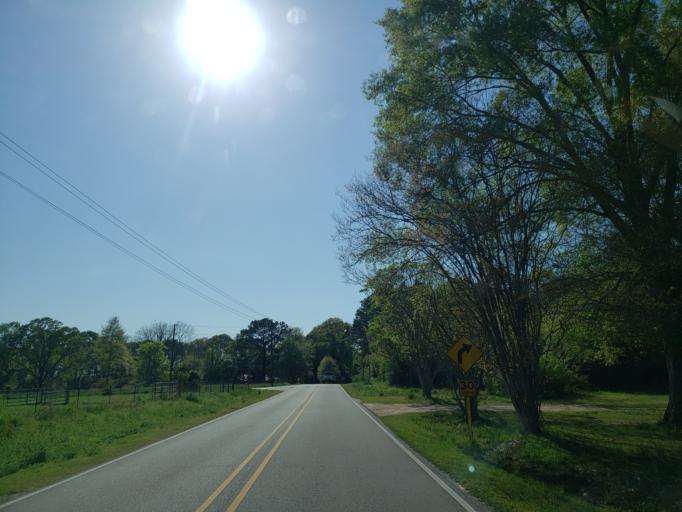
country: US
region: Mississippi
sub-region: Covington County
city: Collins
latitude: 31.6128
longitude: -89.3857
